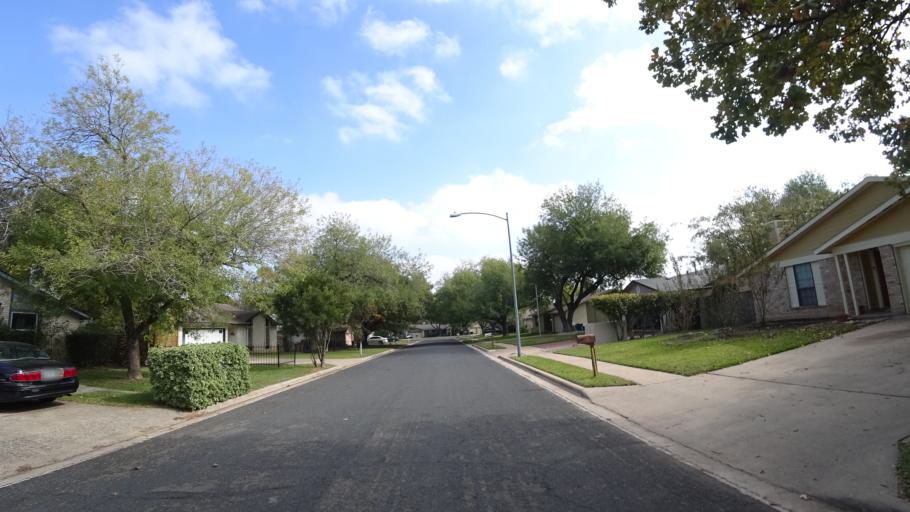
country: US
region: Texas
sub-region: Travis County
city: Shady Hollow
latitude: 30.1988
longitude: -97.8169
